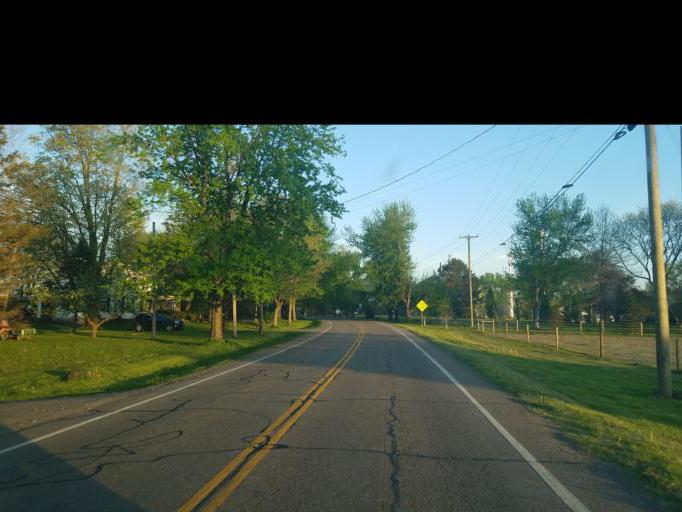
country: US
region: Ohio
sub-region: Trumbull County
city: Cortland
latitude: 41.4256
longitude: -80.5876
